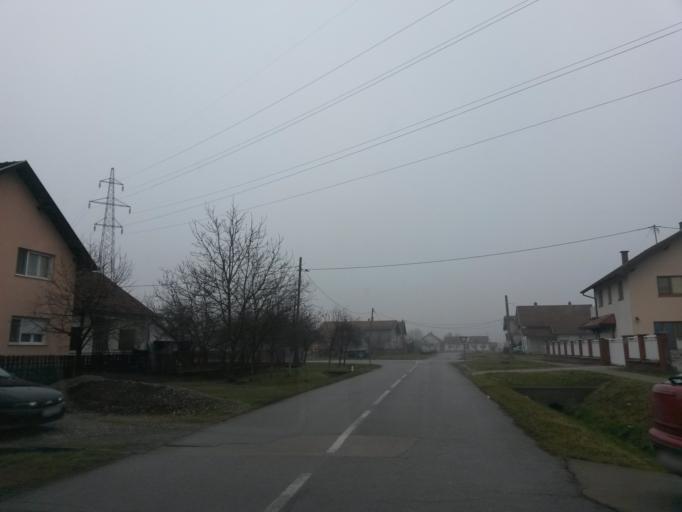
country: HR
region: Vukovarsko-Srijemska
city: Zupanja
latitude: 45.0868
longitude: 18.7006
